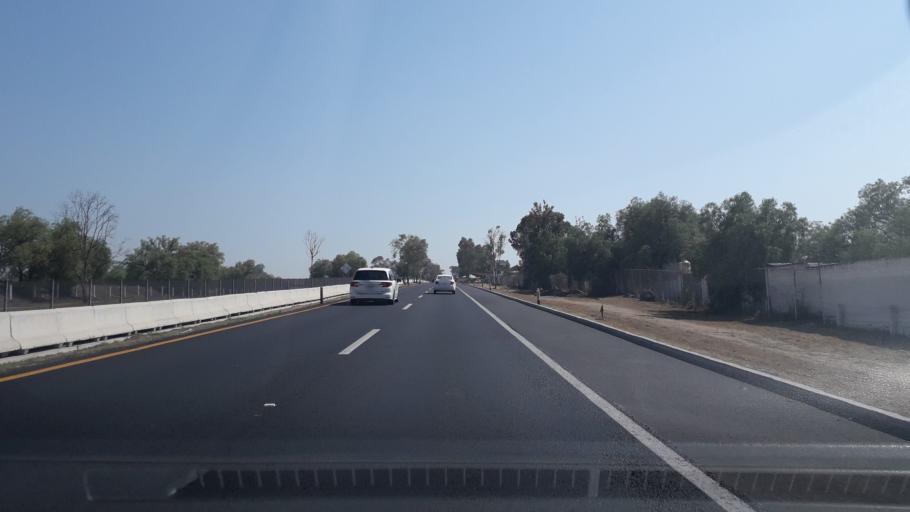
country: MX
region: Mexico
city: Santo Tomas Chiconautla
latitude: 19.6486
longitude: -99.0136
